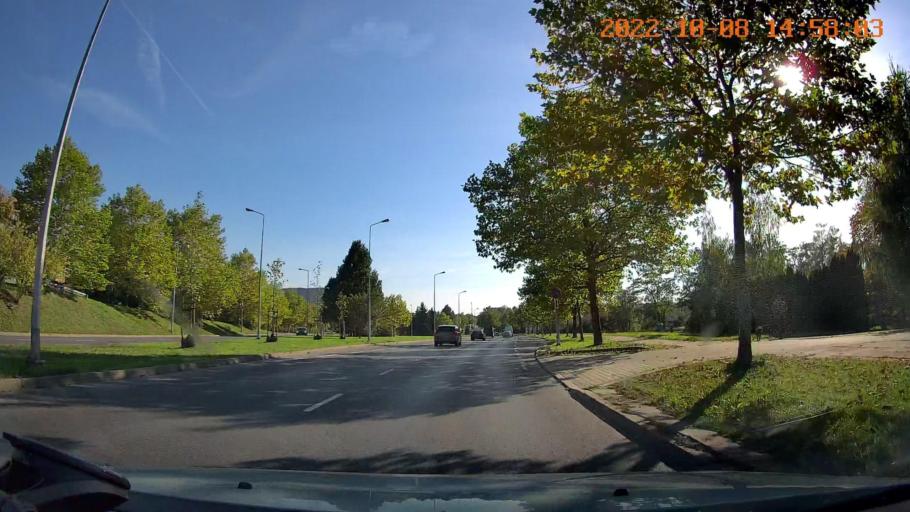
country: PL
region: Lesser Poland Voivodeship
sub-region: Powiat tarnowski
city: Tarnow
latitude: 50.0264
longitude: 20.9981
